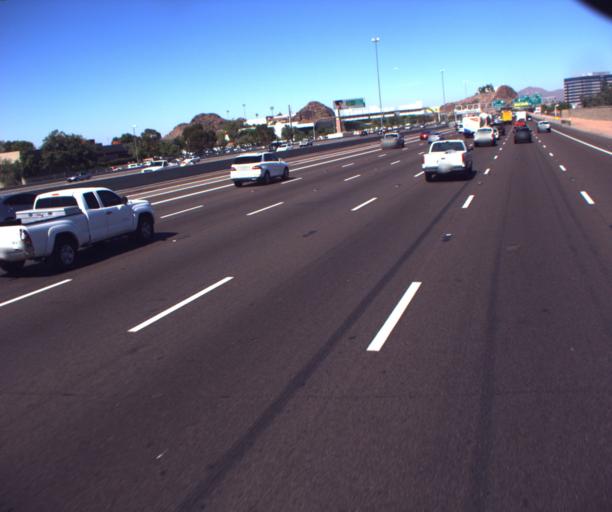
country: US
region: Arizona
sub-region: Maricopa County
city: Guadalupe
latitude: 33.3939
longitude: -111.9673
